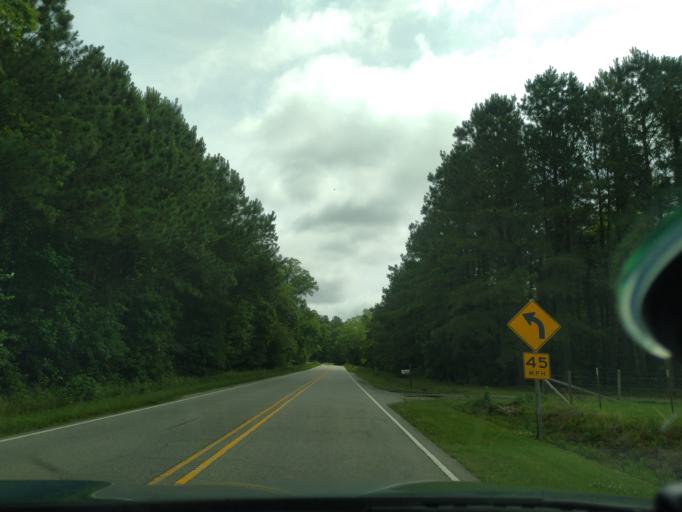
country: US
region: North Carolina
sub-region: Washington County
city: Plymouth
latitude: 35.9062
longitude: -76.6071
